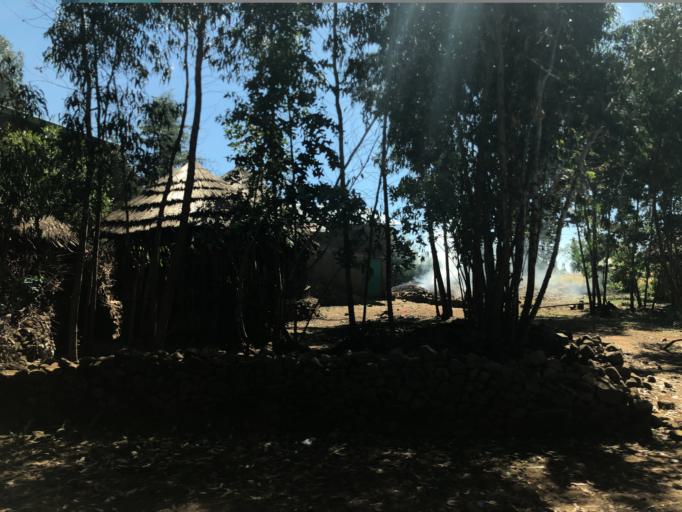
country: ET
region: Amhara
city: Lalibela
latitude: 11.6651
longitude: 38.8505
